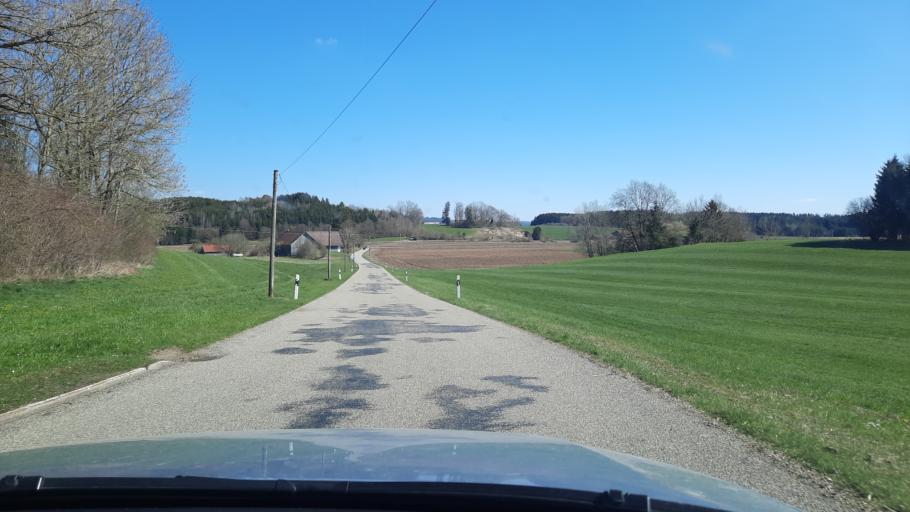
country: DE
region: Bavaria
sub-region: Swabia
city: Wolfertschwenden
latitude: 47.8552
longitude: 10.2479
